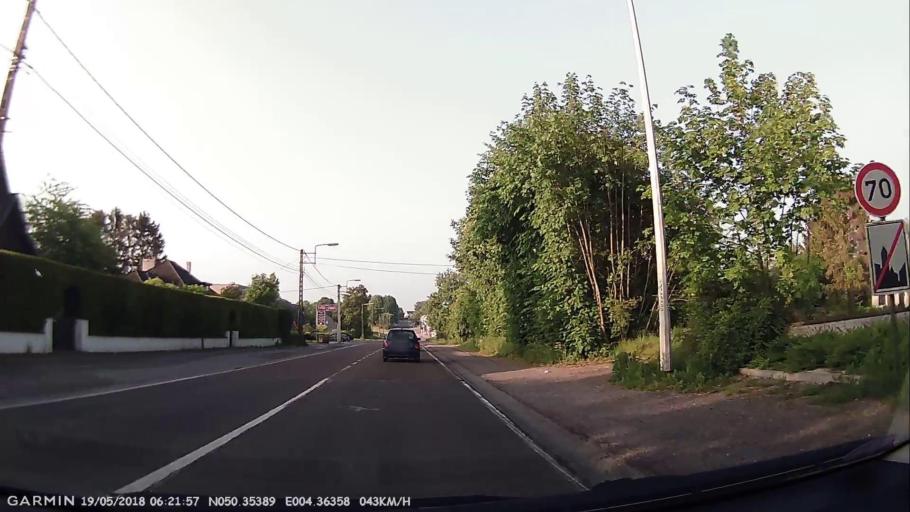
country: BE
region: Wallonia
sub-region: Province du Hainaut
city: Thuin
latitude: 50.3537
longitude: 4.3636
